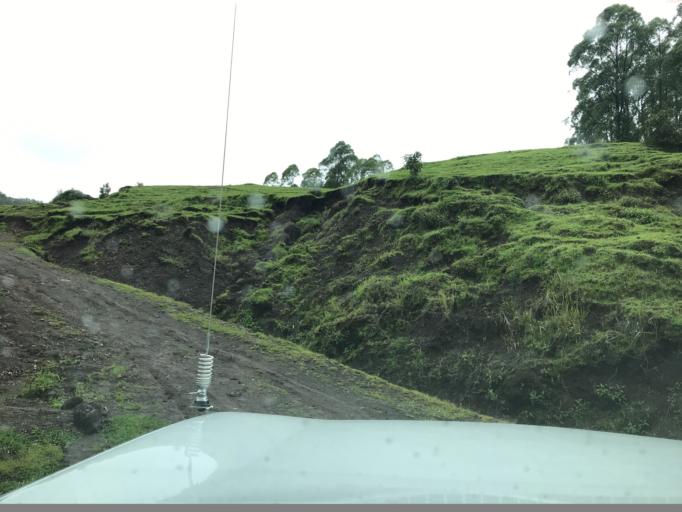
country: TL
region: Ainaro
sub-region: Ainaro
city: Ainaro
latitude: -8.8750
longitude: 125.5509
